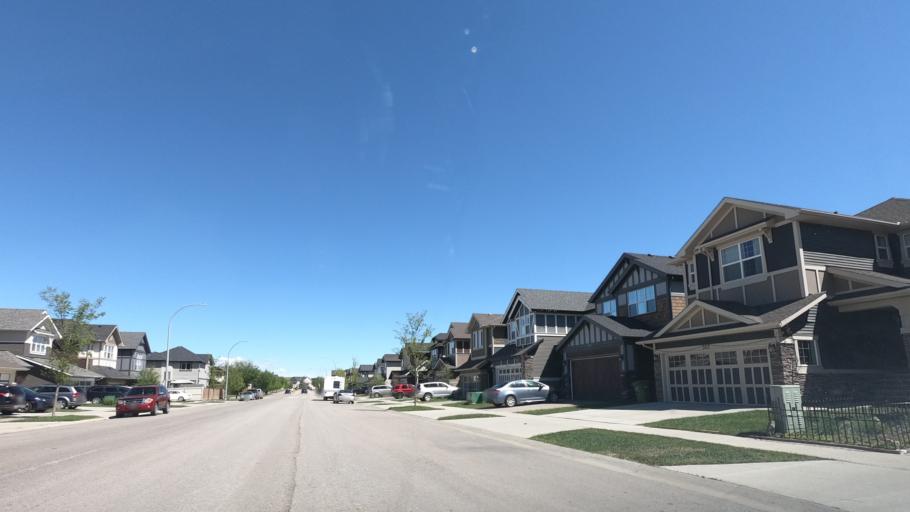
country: CA
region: Alberta
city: Airdrie
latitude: 51.2629
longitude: -113.9848
